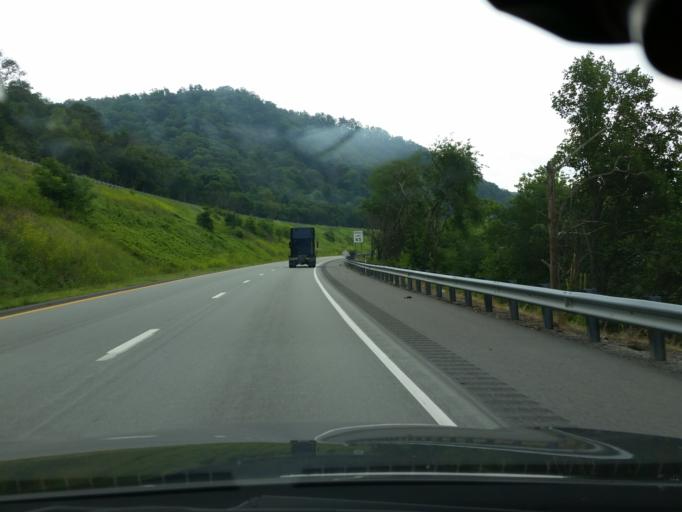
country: US
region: Pennsylvania
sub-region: Perry County
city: Duncannon
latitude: 40.4743
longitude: -77.0358
